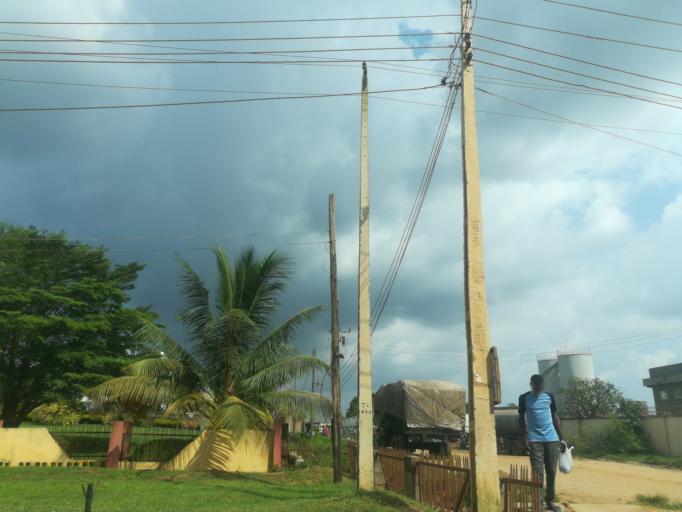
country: NG
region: Oyo
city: Ibadan
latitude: 7.3622
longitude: 3.8458
